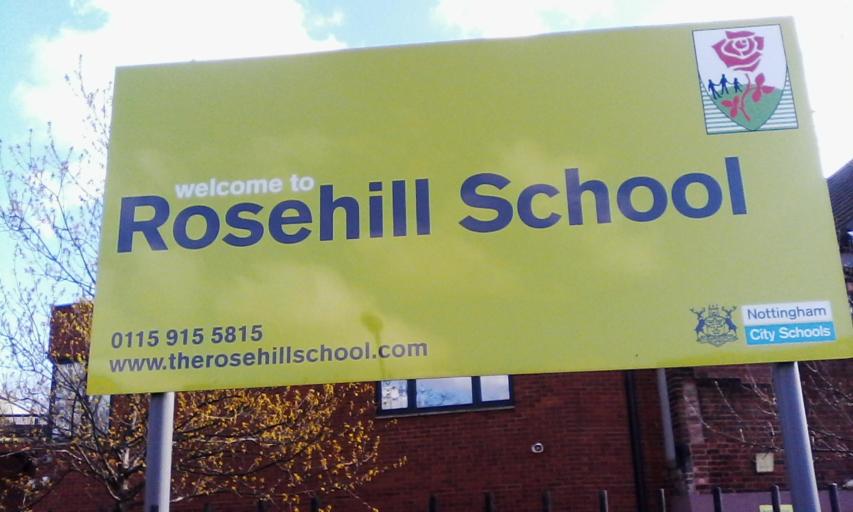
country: GB
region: England
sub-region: Nottingham
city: Nottingham
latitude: 52.9598
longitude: -1.1310
